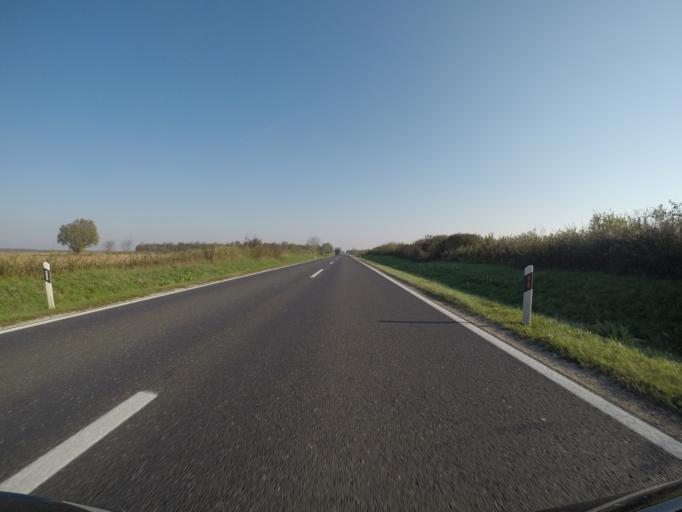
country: HR
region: Koprivnicko-Krizevacka
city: Kalinovac
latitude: 46.0082
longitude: 17.1037
